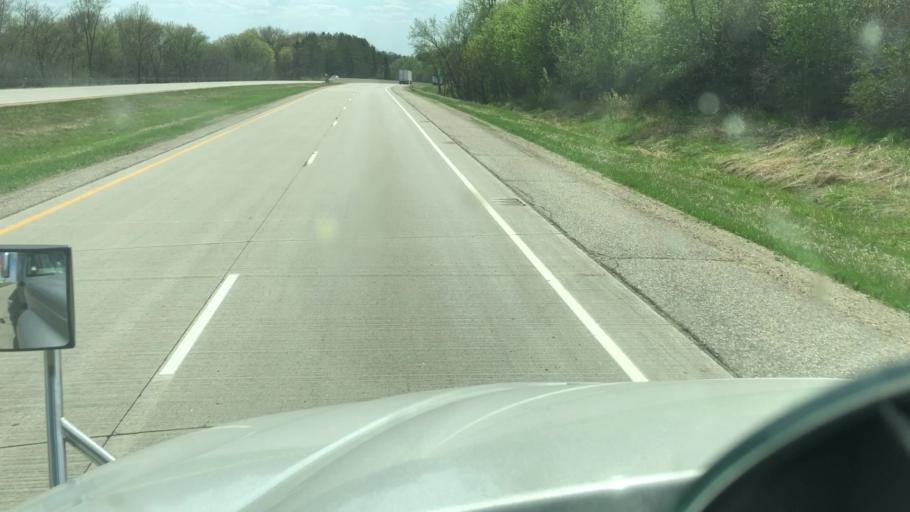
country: US
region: Minnesota
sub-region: Le Sueur County
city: Le Sueur
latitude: 44.4891
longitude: -93.8774
